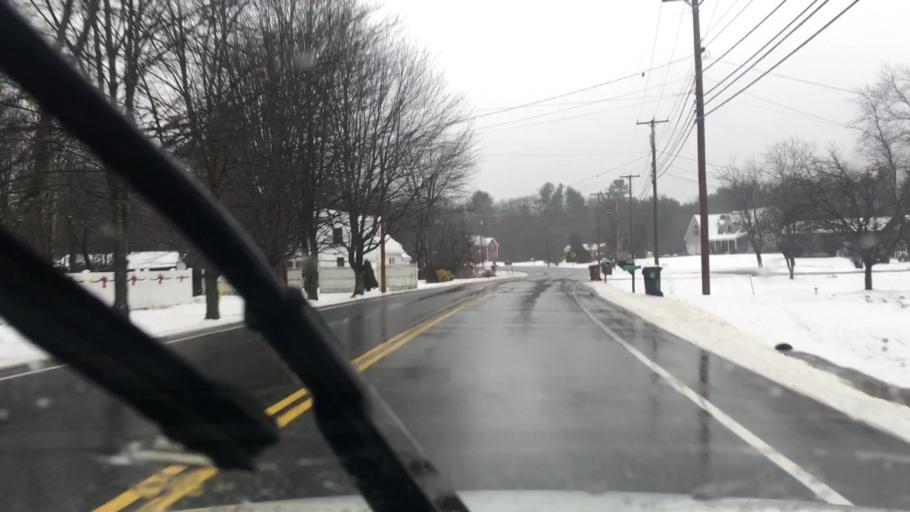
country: US
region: Maine
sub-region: York County
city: Biddeford
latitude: 43.5469
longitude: -70.4881
